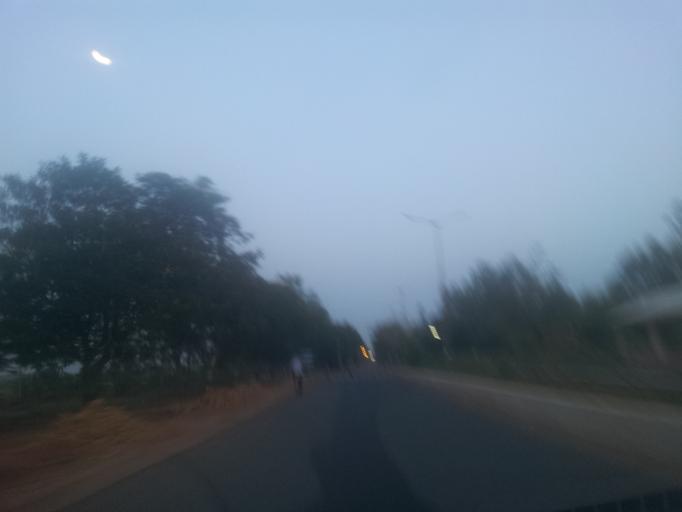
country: IN
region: Tamil Nadu
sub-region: Cuddalore
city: Kurinjippadi
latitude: 11.6191
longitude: 79.5333
